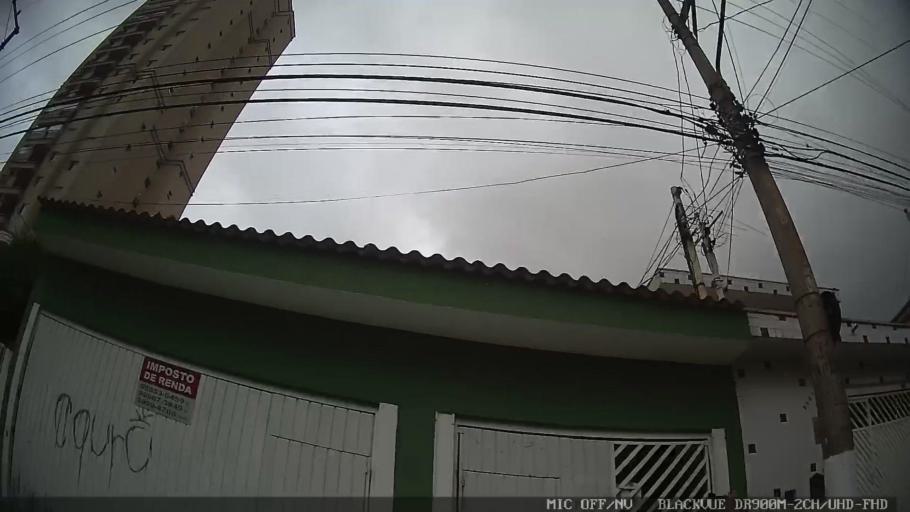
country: BR
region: Sao Paulo
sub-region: Osasco
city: Osasco
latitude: -23.4909
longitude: -46.7148
